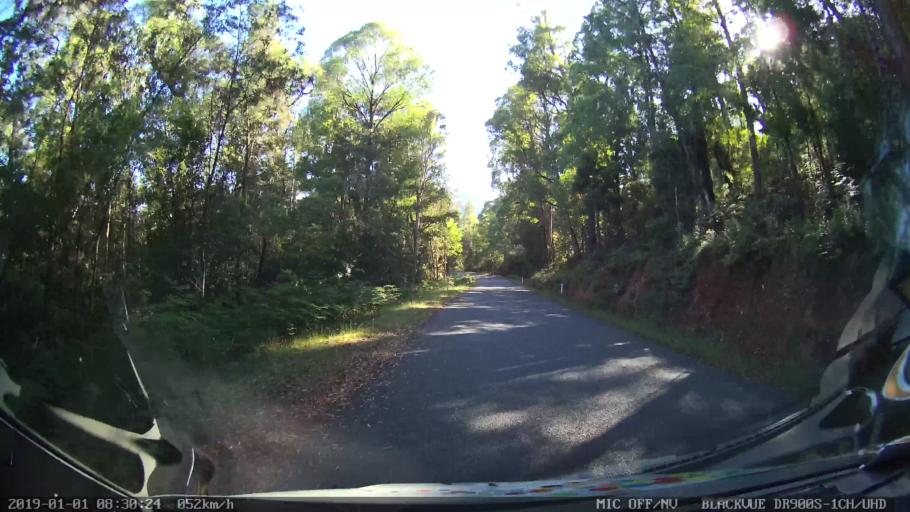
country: AU
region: New South Wales
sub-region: Snowy River
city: Jindabyne
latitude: -36.3760
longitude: 148.1979
